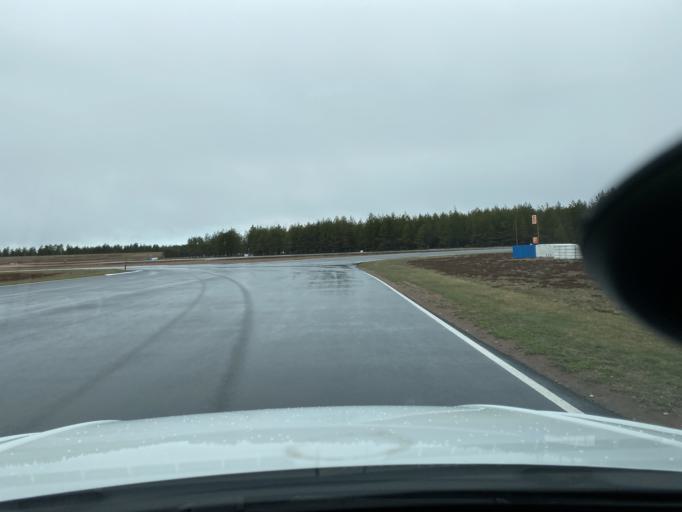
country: FI
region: Satakunta
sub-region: Pori
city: Vampula
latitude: 60.9774
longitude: 22.6667
